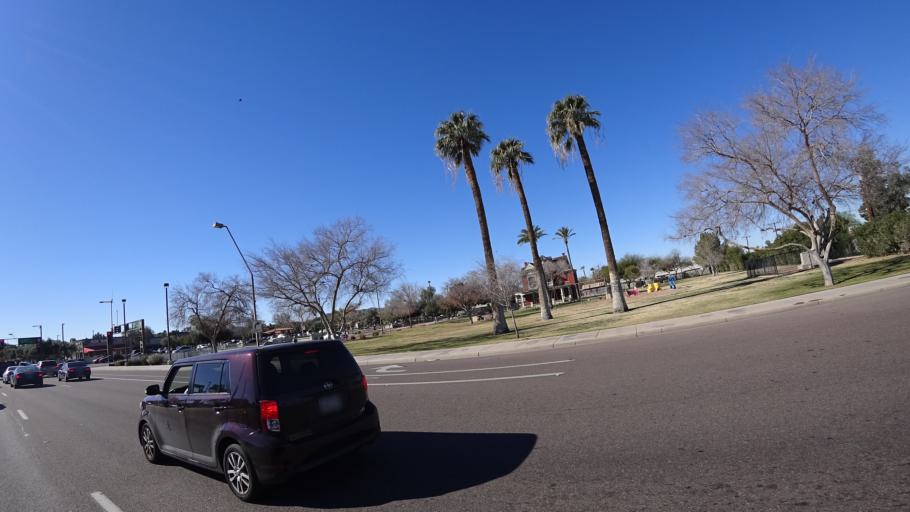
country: US
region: Arizona
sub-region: Maricopa County
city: Guadalupe
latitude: 33.3936
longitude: -111.9608
